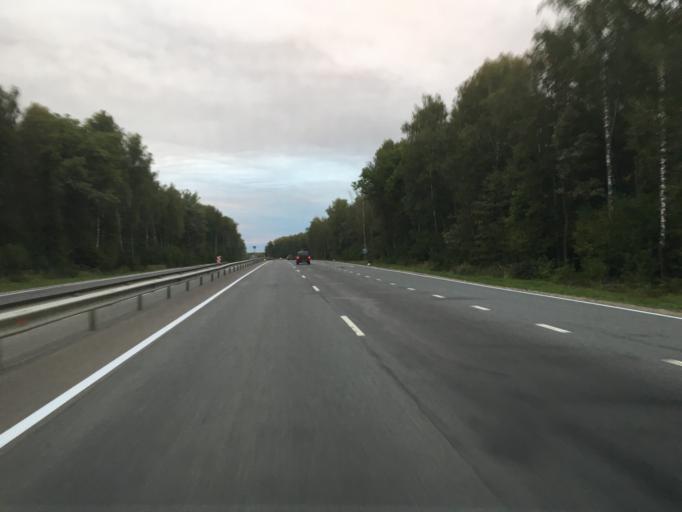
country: RU
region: Kaluga
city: Kaluga
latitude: 54.5766
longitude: 36.3354
